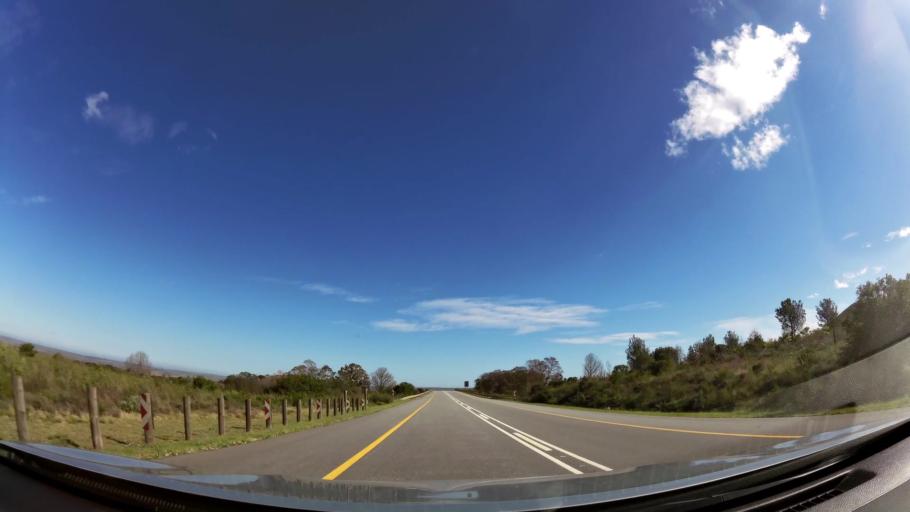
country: ZA
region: Eastern Cape
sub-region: Cacadu District Municipality
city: Kruisfontein
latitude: -33.9970
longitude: 24.6888
